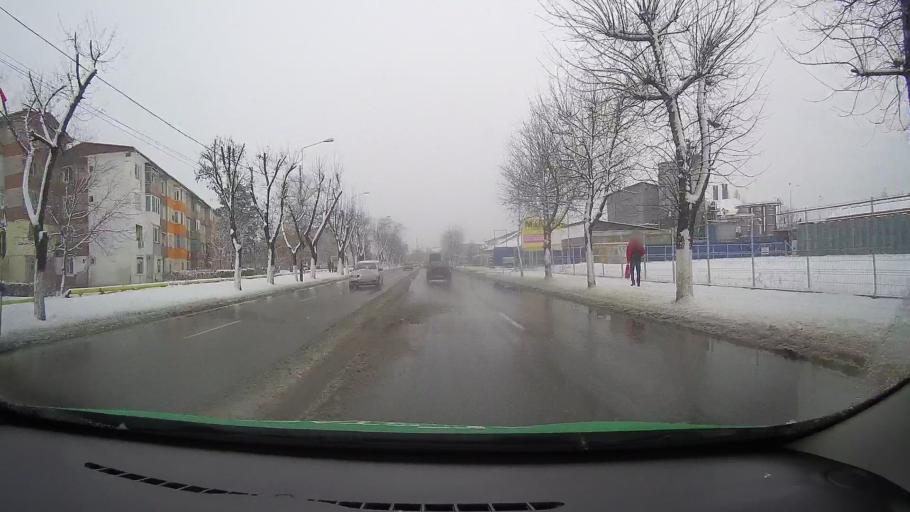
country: RO
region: Hunedoara
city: Hunedoara
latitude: 45.7658
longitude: 22.9051
